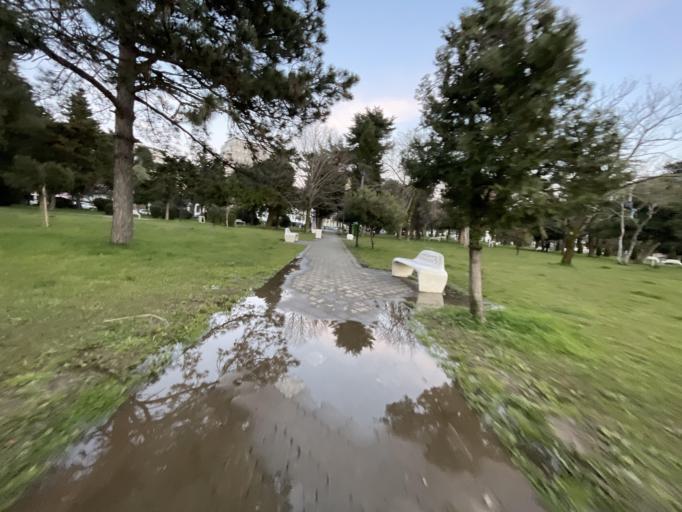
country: GE
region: Ajaria
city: Batumi
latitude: 41.6487
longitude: 41.6284
